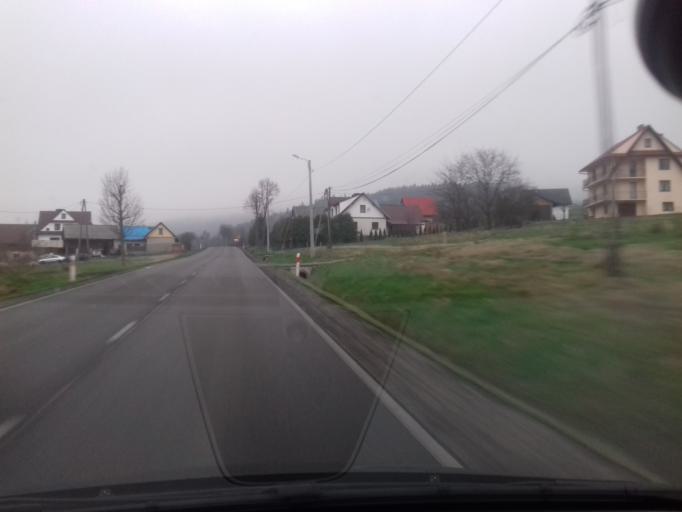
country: PL
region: Lesser Poland Voivodeship
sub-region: Powiat limanowski
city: Dobra
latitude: 49.7021
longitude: 20.2278
